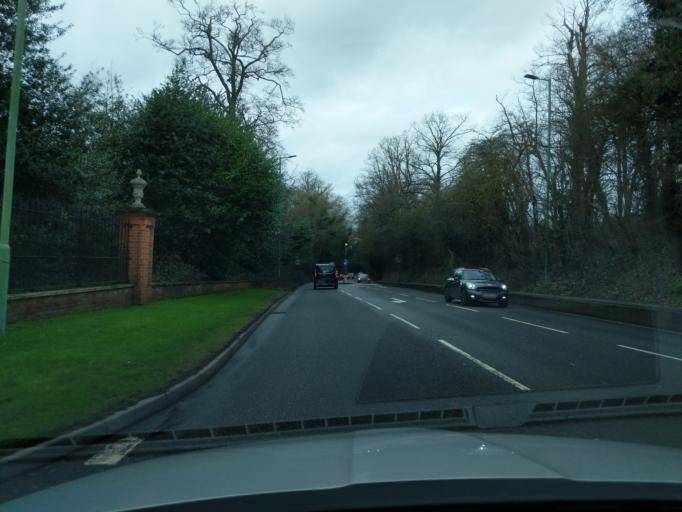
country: GB
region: England
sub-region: Hertfordshire
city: Abbots Langley
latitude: 51.6778
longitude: -0.4249
